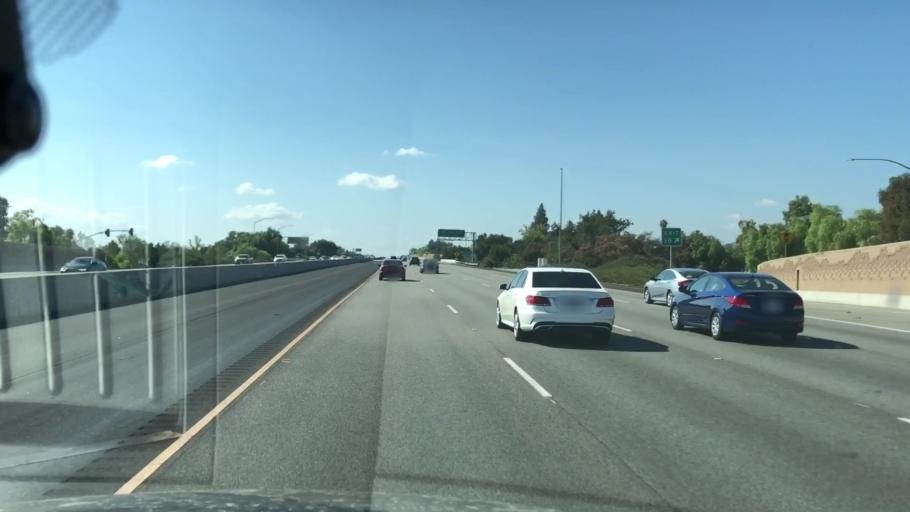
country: US
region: California
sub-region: Ventura County
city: Santa Susana
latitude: 34.2819
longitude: -118.6880
